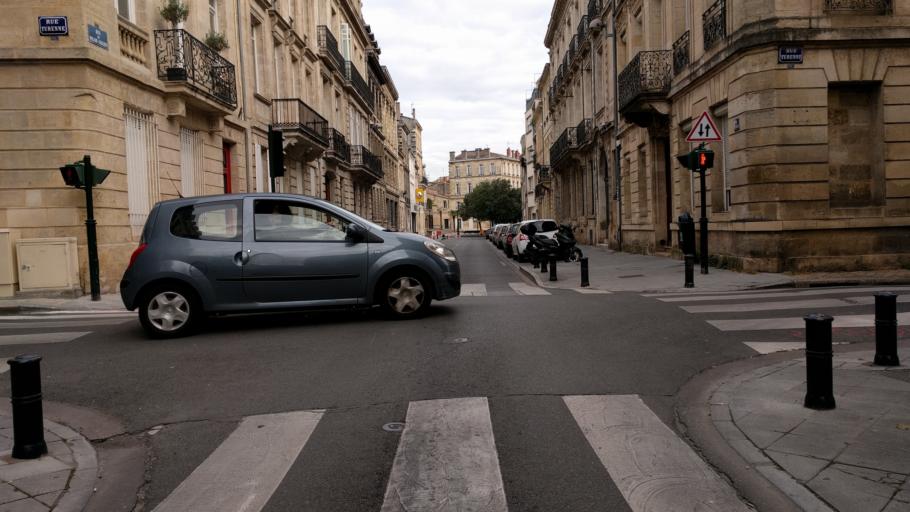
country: FR
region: Aquitaine
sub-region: Departement de la Gironde
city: Bordeaux
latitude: 44.8457
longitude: -0.5819
